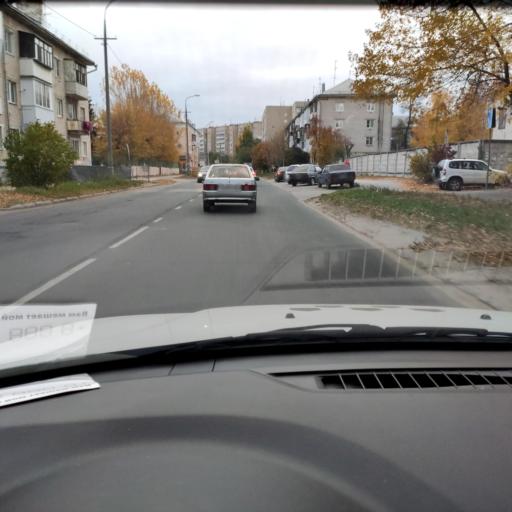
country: RU
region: Samara
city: Tol'yatti
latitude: 53.5047
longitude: 49.4000
